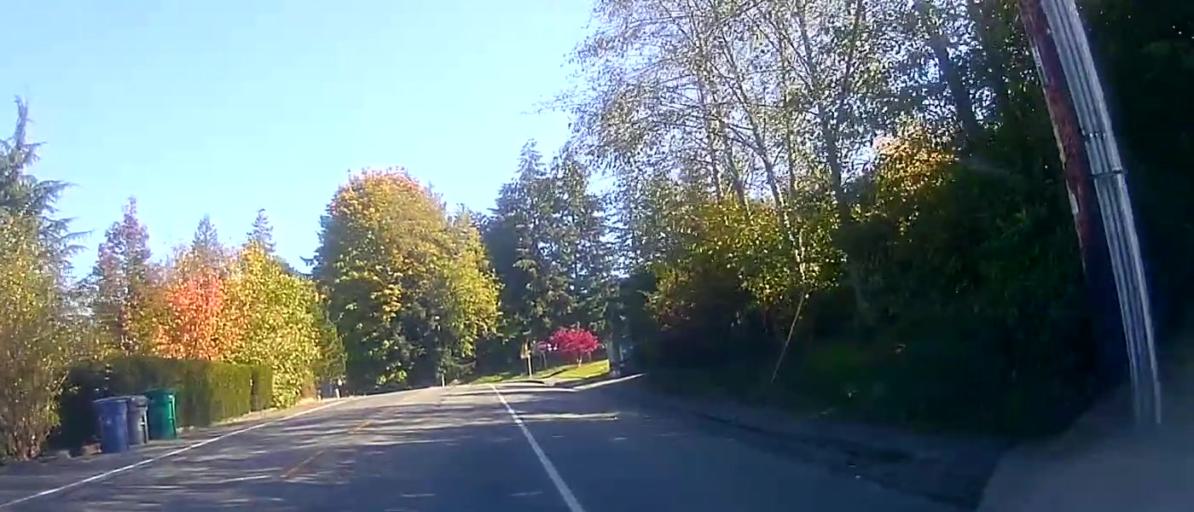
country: US
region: Washington
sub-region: Skagit County
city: Mount Vernon
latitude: 48.4282
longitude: -122.2928
